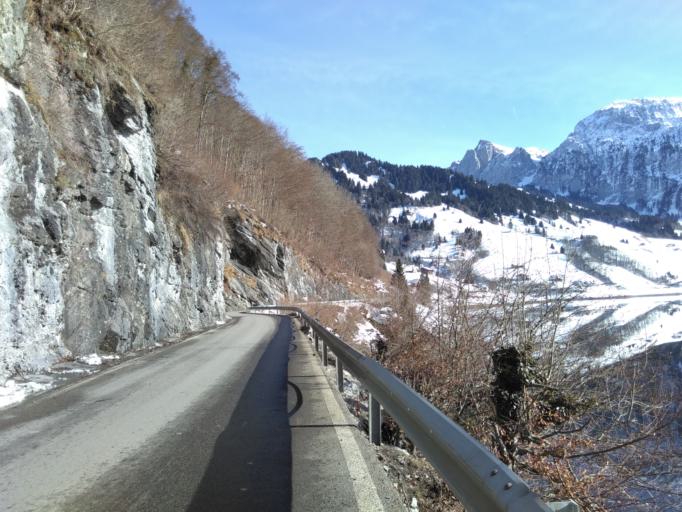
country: CH
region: Schwyz
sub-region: Bezirk March
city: Vorderthal
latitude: 47.1069
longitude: 8.9068
